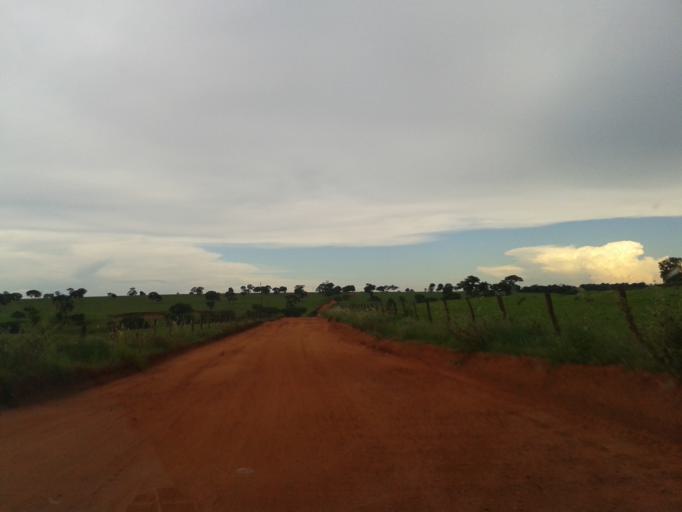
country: BR
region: Minas Gerais
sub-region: Santa Vitoria
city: Santa Vitoria
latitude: -19.1040
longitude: -50.5102
